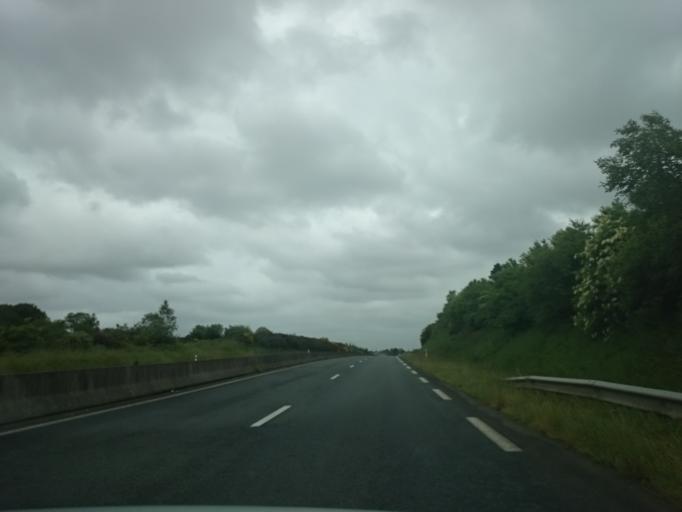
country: FR
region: Brittany
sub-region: Departement des Cotes-d'Armor
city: Ploubezre
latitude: 48.7207
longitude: -3.4210
